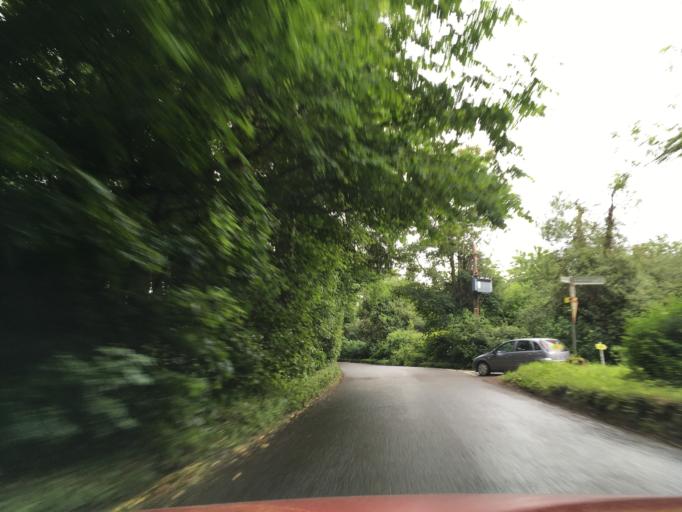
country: GB
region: England
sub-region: Gloucestershire
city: Tetbury
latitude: 51.6053
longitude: -2.1880
